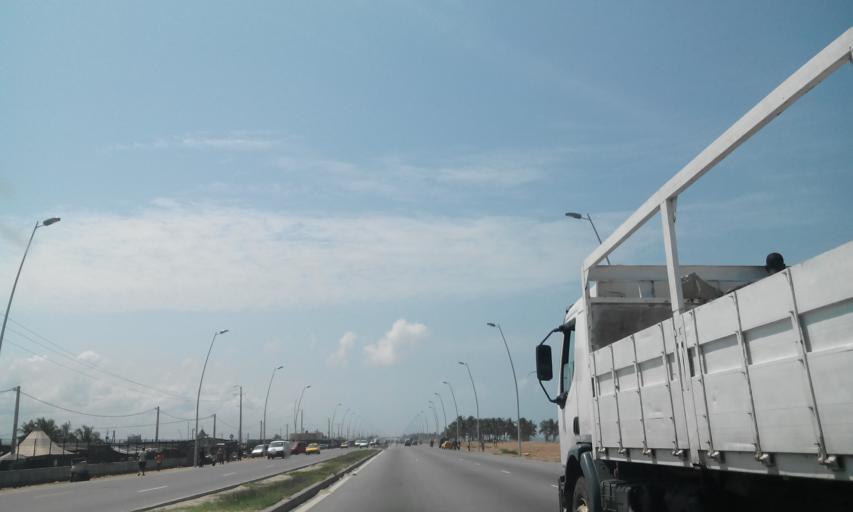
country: CI
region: Lagunes
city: Bingerville
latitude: 5.2419
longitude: -3.9131
